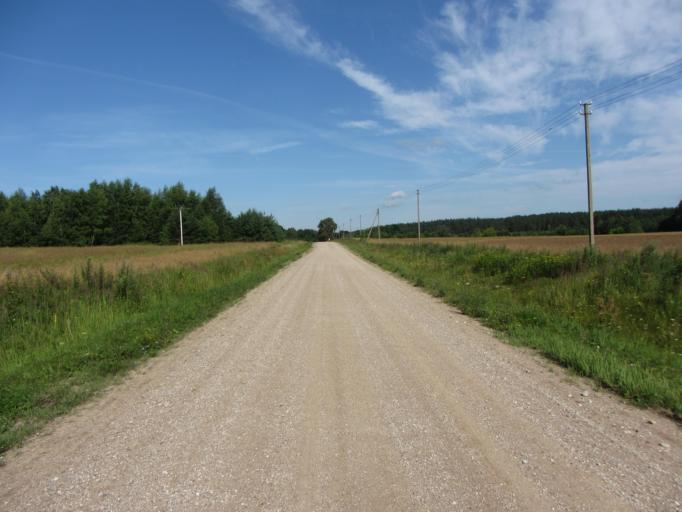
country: LT
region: Vilnius County
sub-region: Vilniaus Rajonas
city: Vievis
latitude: 54.8777
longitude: 24.8297
